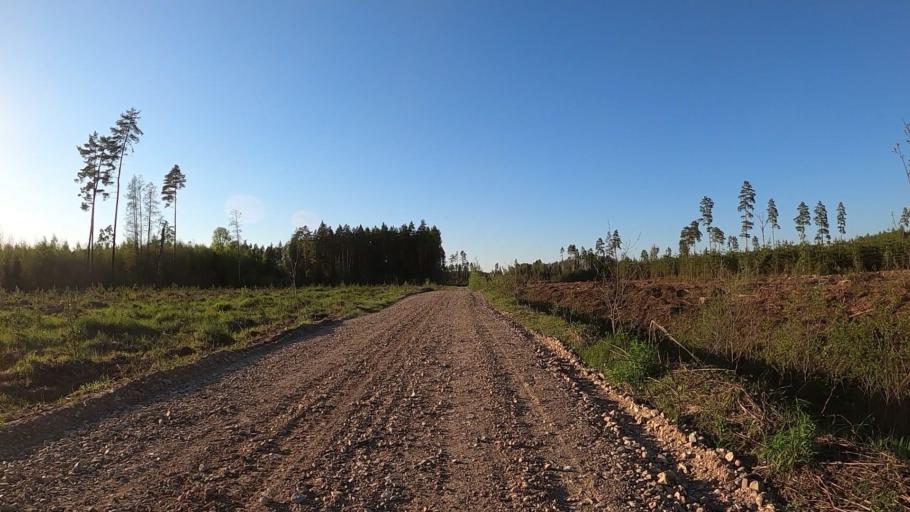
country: LV
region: Kekava
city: Kekava
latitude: 56.7711
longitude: 24.2227
